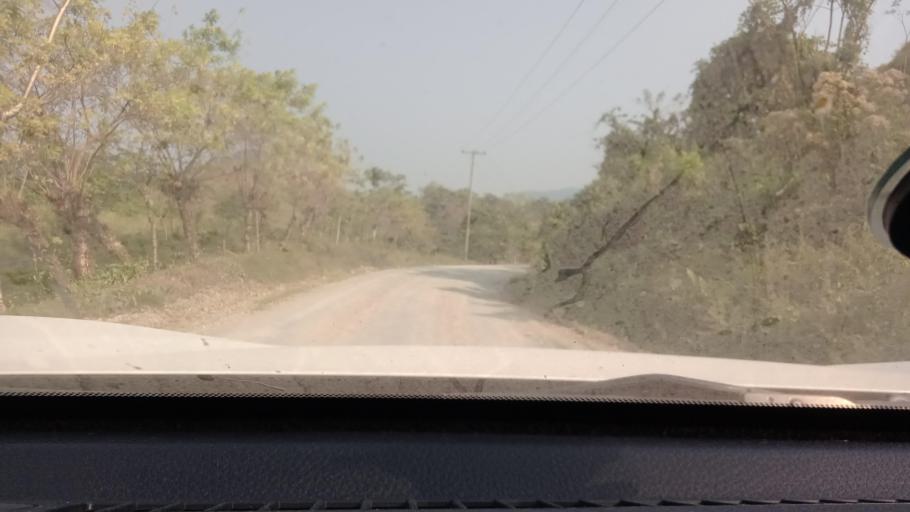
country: MX
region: Tabasco
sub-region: Huimanguillo
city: Francisco Rueda
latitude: 17.6155
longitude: -93.9395
